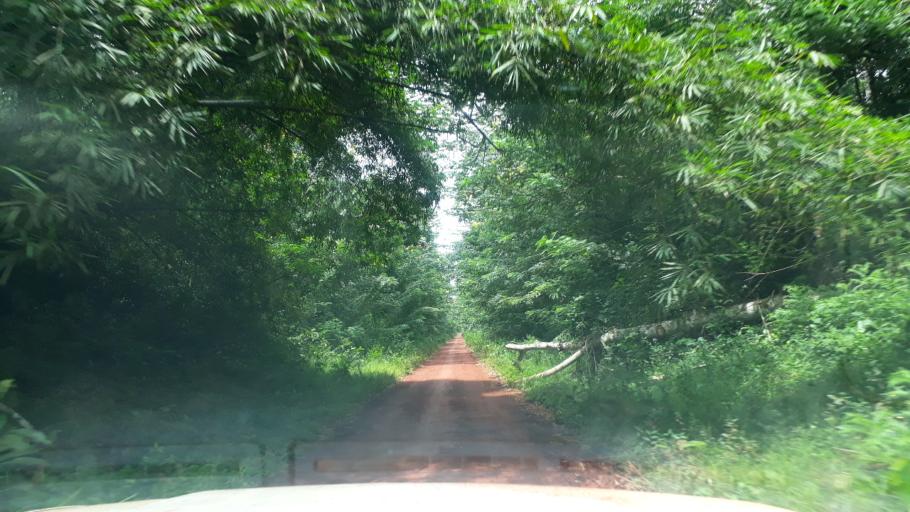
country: CD
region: Eastern Province
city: Aketi
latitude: 2.9275
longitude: 24.0860
